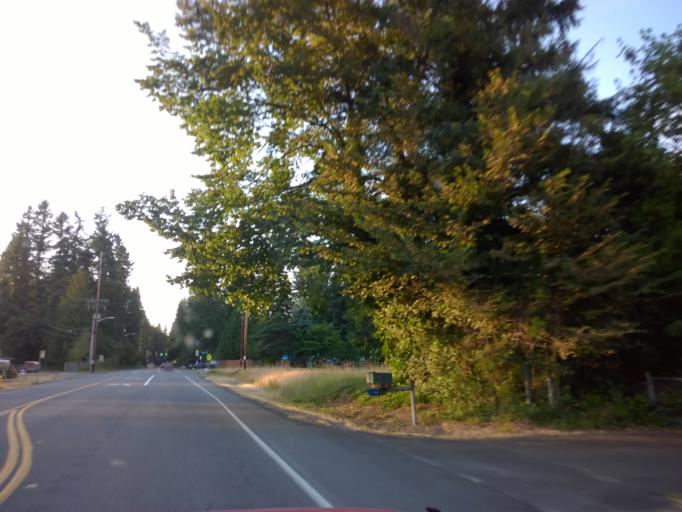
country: US
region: Washington
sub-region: King County
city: Cottage Lake
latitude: 47.7429
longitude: -122.0809
